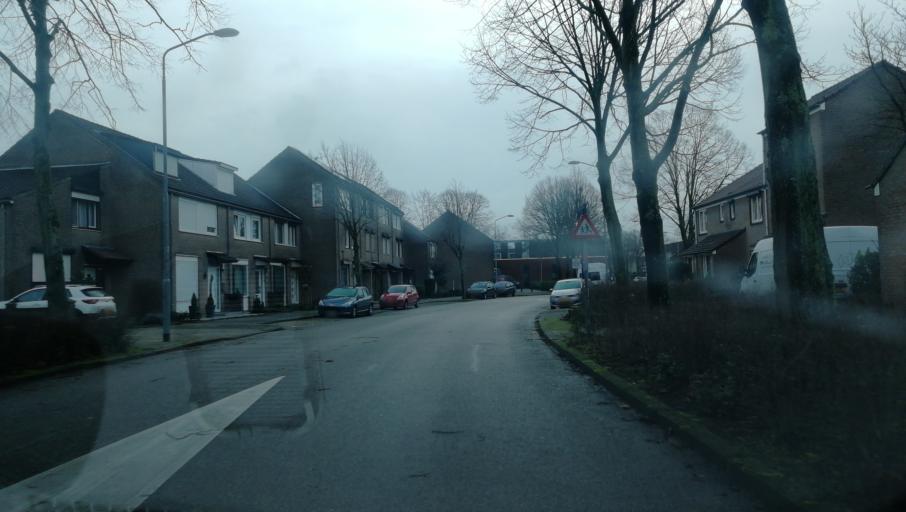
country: NL
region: Limburg
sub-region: Gemeente Venlo
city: Tegelen
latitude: 51.3673
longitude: 6.1290
